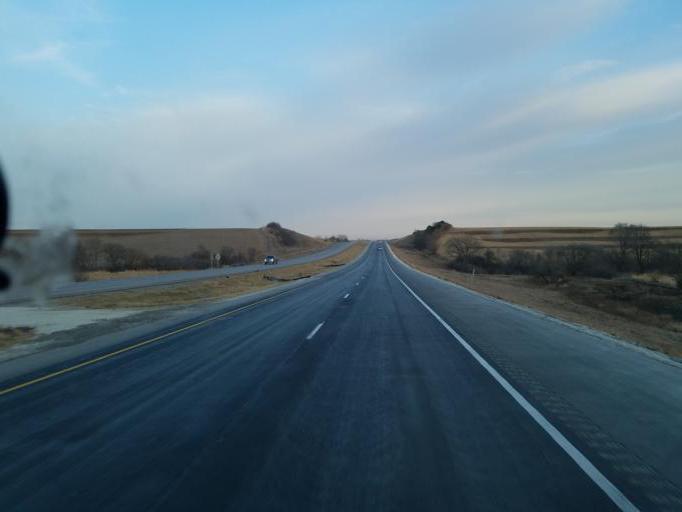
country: US
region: Iowa
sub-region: Harrison County
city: Missouri Valley
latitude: 41.4986
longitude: -95.7576
